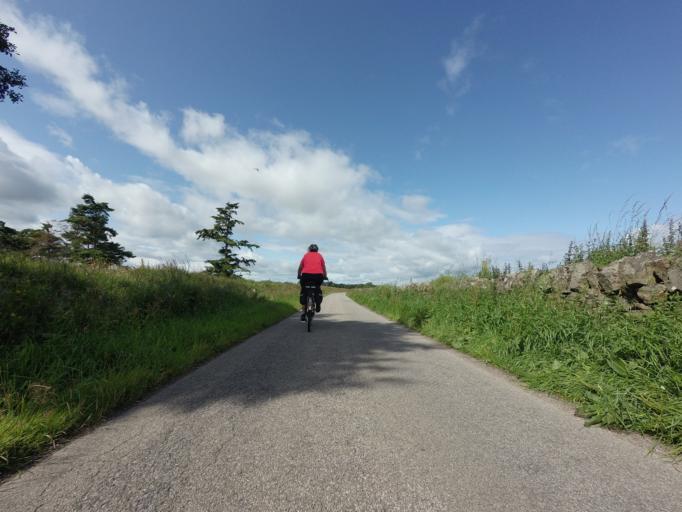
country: GB
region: Scotland
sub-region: Moray
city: Burghead
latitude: 57.6542
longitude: -3.4559
